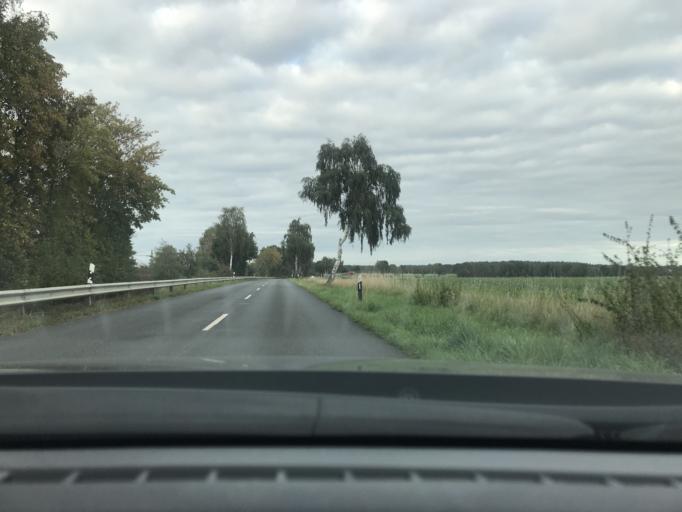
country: DE
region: Lower Saxony
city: Suderburg
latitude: 52.9083
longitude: 10.4374
